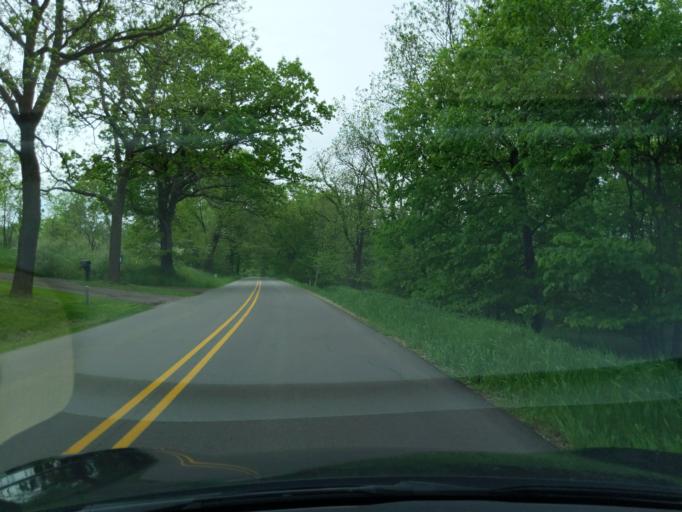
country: US
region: Michigan
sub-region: Ingham County
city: Leslie
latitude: 42.4219
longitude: -84.3561
